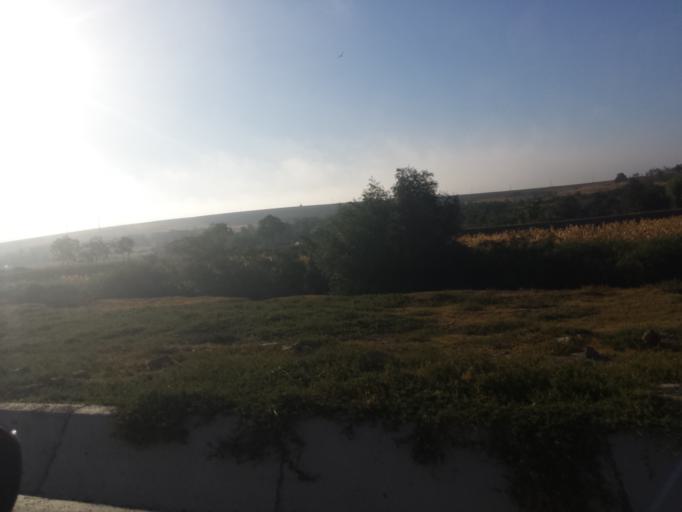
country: RO
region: Constanta
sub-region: Comuna Saraiu
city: Saraiu
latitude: 44.7228
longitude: 28.1609
